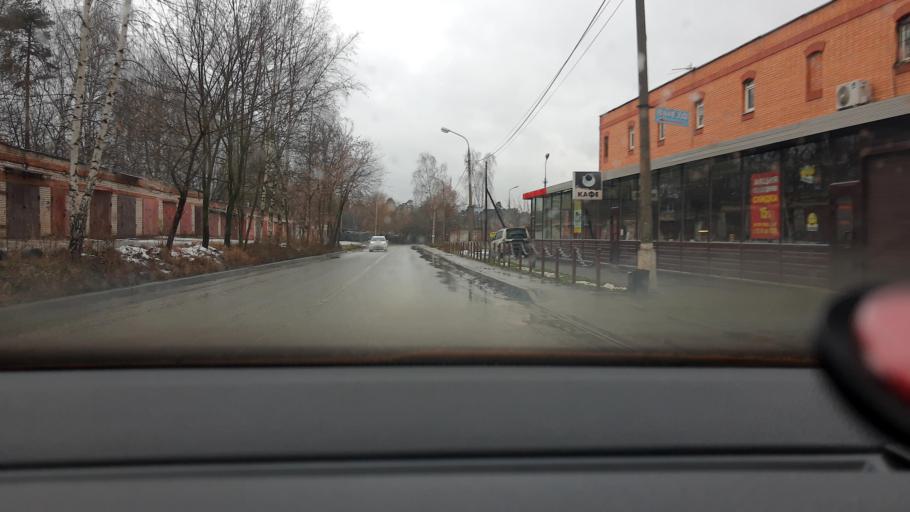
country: RU
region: Moskovskaya
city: Bolshevo
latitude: 55.9295
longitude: 37.8268
